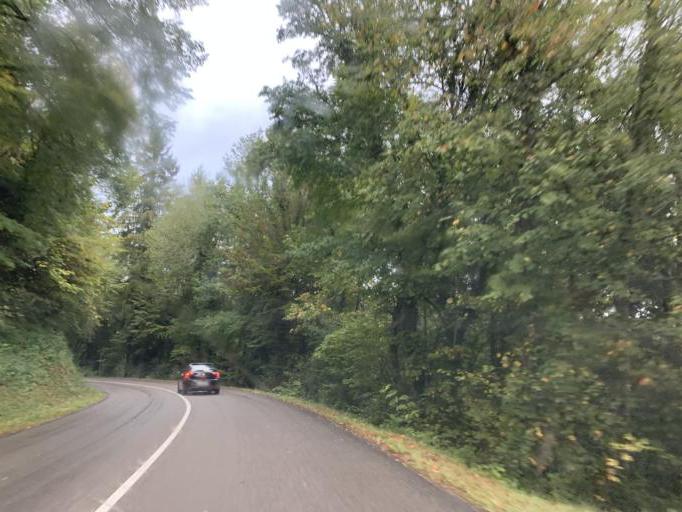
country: FR
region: Rhone-Alpes
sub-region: Departement de l'Ain
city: Belley
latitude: 45.7066
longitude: 5.6536
